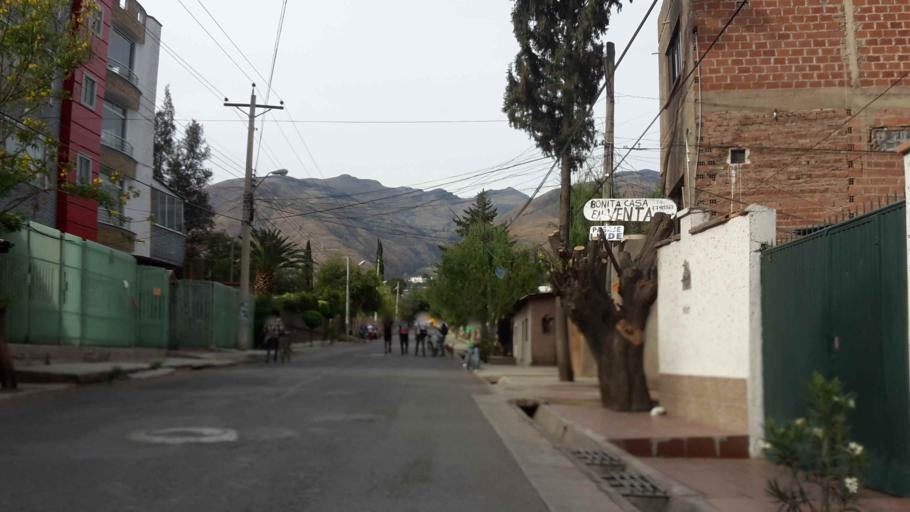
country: BO
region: Cochabamba
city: Cochabamba
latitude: -17.3538
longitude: -66.1941
